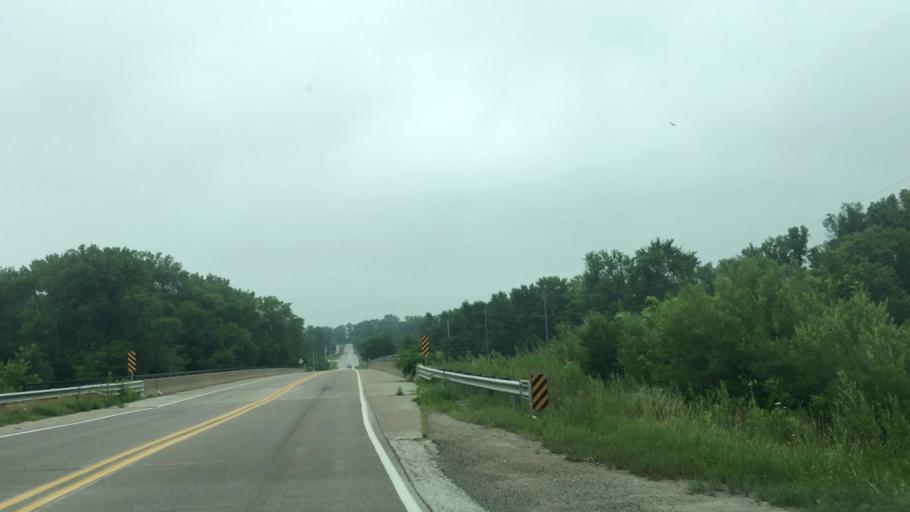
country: US
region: Iowa
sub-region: Johnson County
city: Iowa City
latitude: 41.6930
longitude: -91.5473
